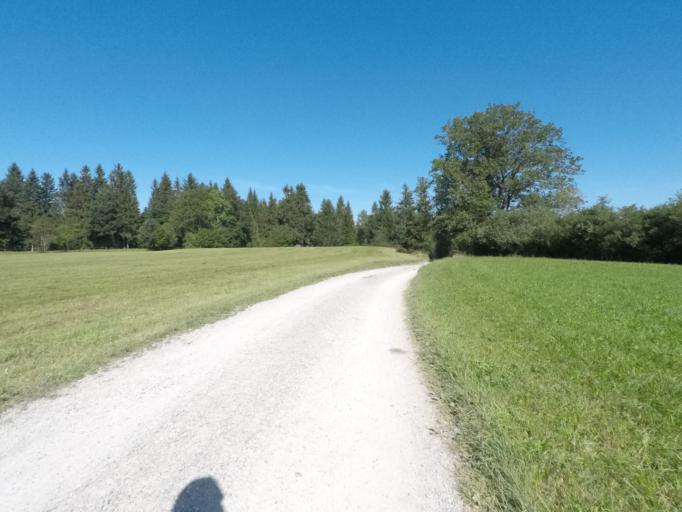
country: DE
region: Bavaria
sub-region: Upper Bavaria
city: Gaissach
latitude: 47.7397
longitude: 11.5890
